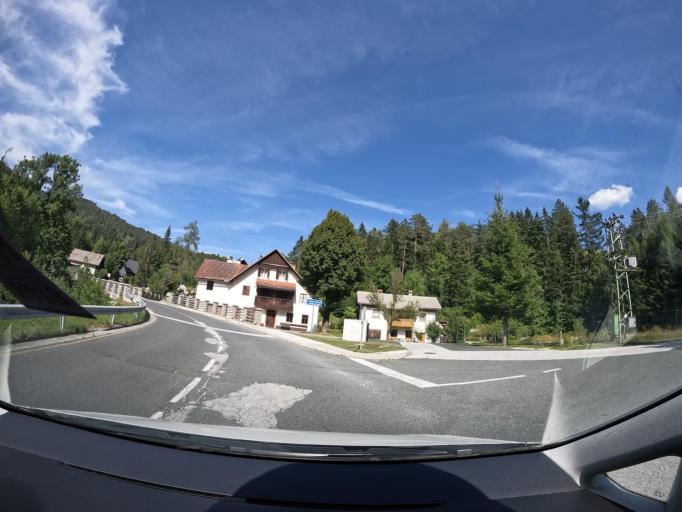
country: AT
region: Carinthia
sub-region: Politischer Bezirk Klagenfurt Land
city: Moosburg
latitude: 46.6558
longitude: 14.1349
